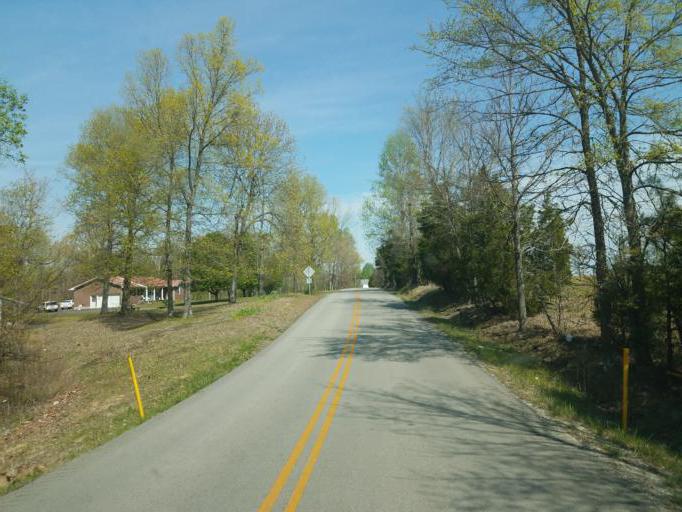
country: US
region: Kentucky
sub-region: Edmonson County
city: Brownsville
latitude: 37.3003
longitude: -86.2488
